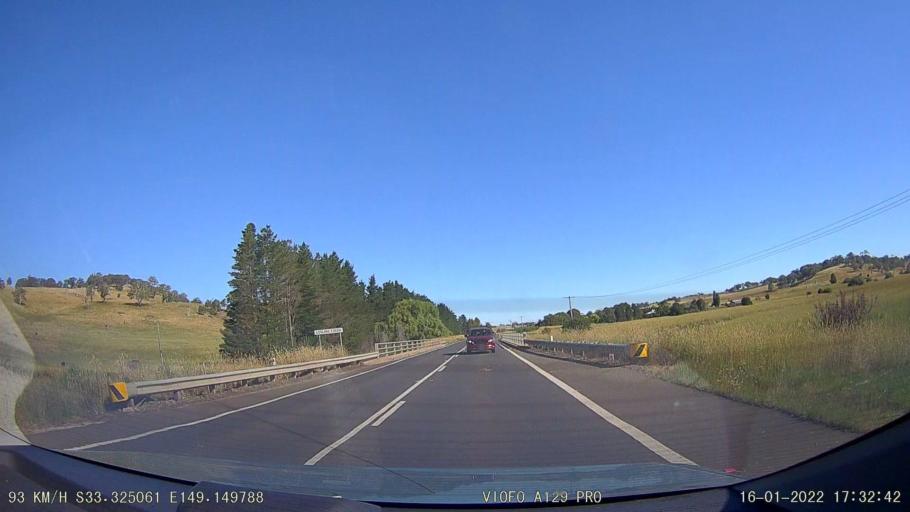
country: AU
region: New South Wales
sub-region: Orange Municipality
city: Orange
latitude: -33.3250
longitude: 149.1497
